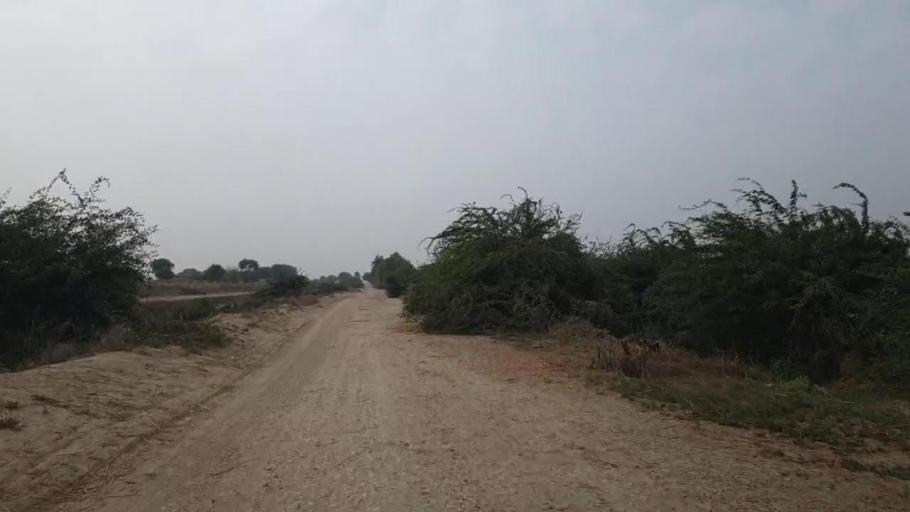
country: PK
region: Sindh
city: Kario
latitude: 24.9012
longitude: 68.5296
